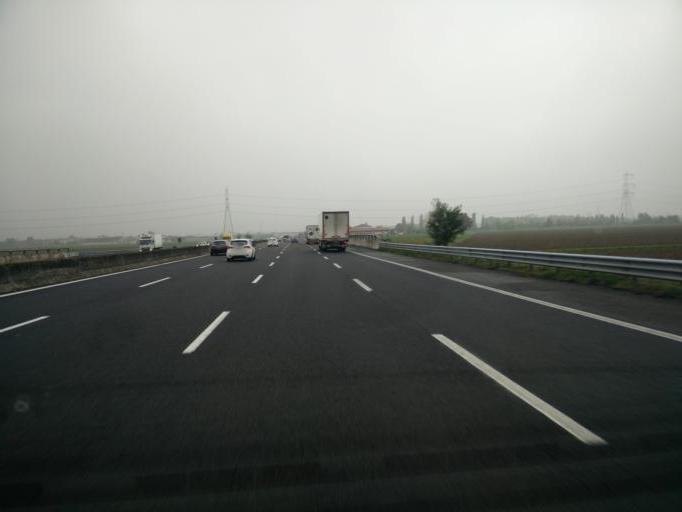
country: IT
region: Emilia-Romagna
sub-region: Provincia di Modena
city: San Damaso
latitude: 44.5864
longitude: 10.9601
